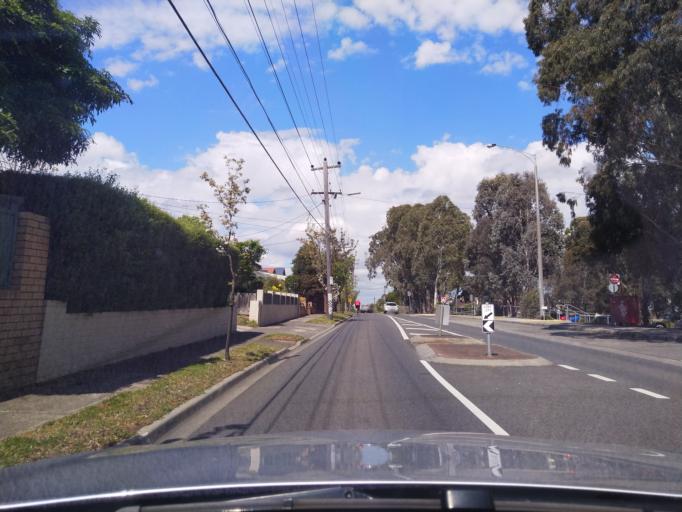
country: AU
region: Victoria
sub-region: Banyule
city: Bellfield
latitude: -37.7620
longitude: 145.0441
